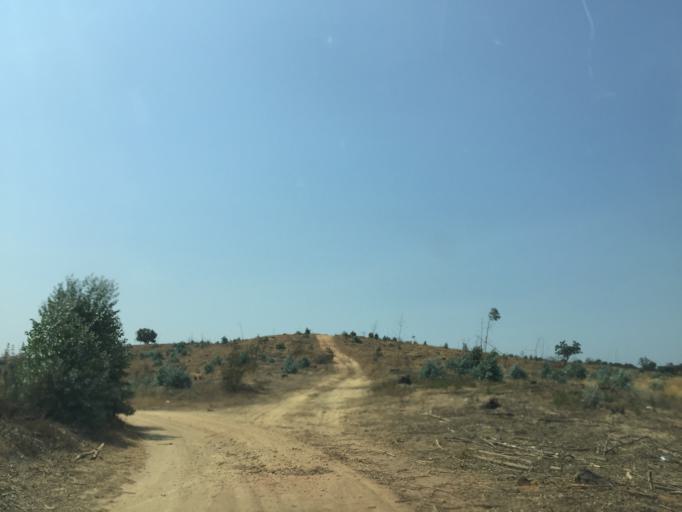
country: PT
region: Setubal
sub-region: Grandola
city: Grandola
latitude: 38.0478
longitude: -8.4674
